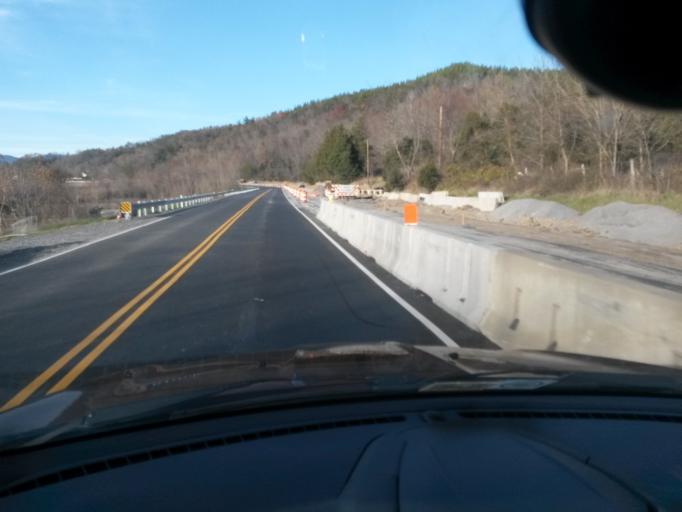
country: US
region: Virginia
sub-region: Alleghany County
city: Clifton Forge
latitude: 37.6688
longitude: -79.7960
